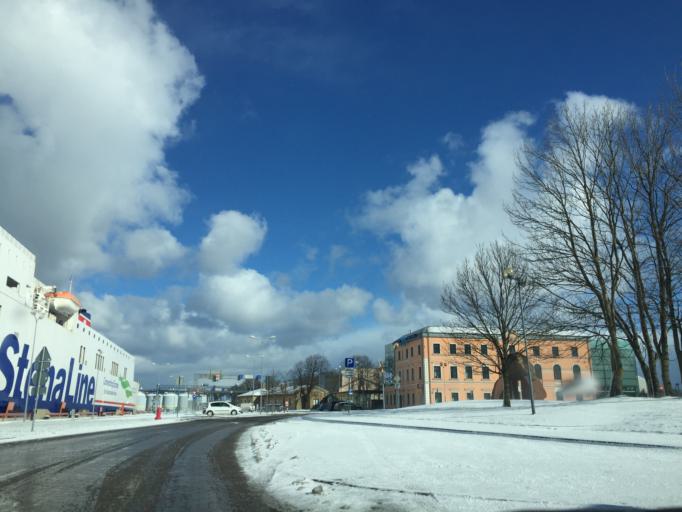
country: LV
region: Ventspils
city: Ventspils
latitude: 57.3987
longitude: 21.5678
